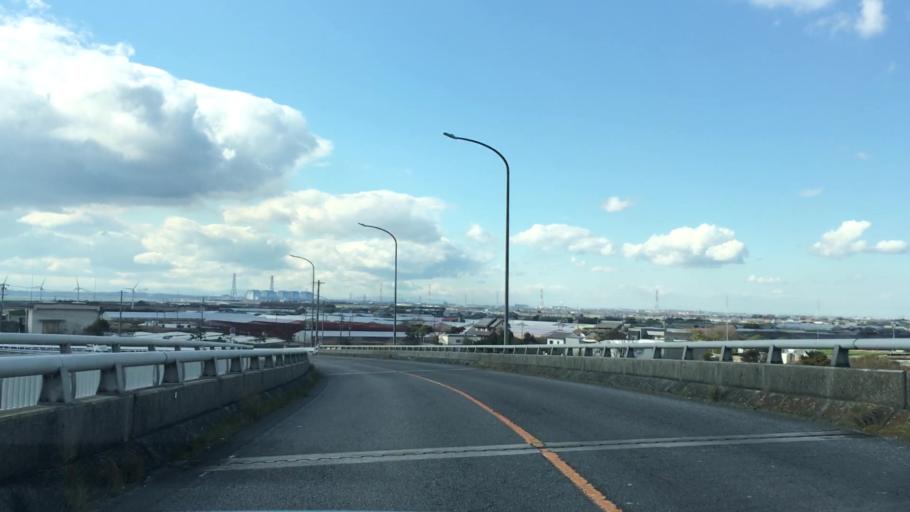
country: JP
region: Aichi
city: Ishiki
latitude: 34.7949
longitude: 137.0177
